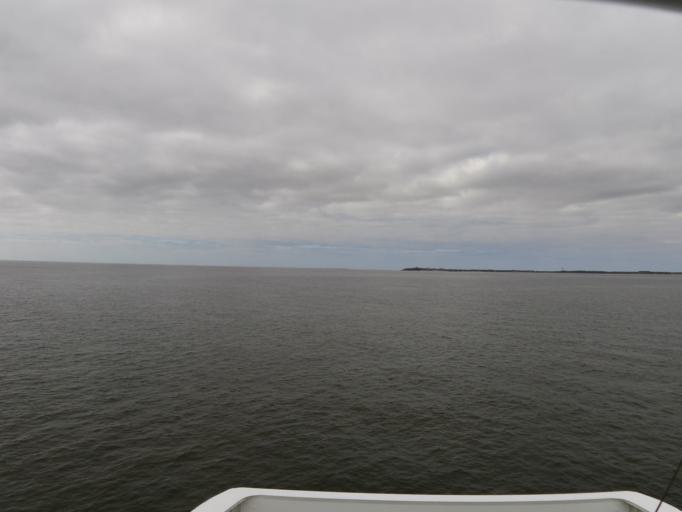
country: DE
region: Schleswig-Holstein
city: Witsum
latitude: 54.6418
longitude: 8.4498
